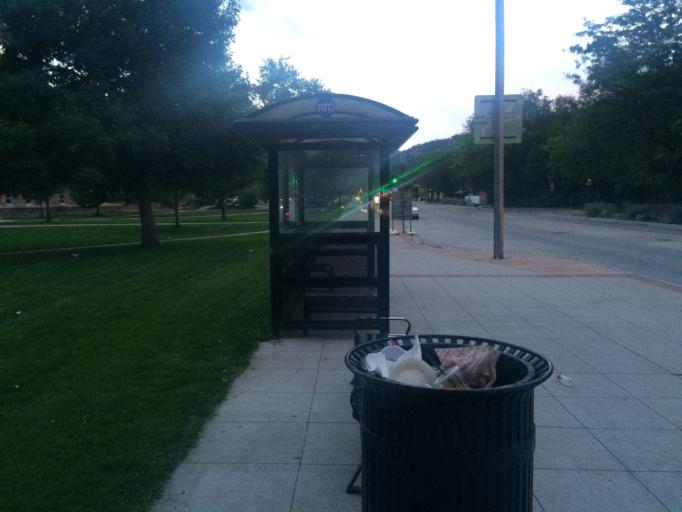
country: US
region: Colorado
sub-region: Boulder County
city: Boulder
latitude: 40.0145
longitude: -105.2730
